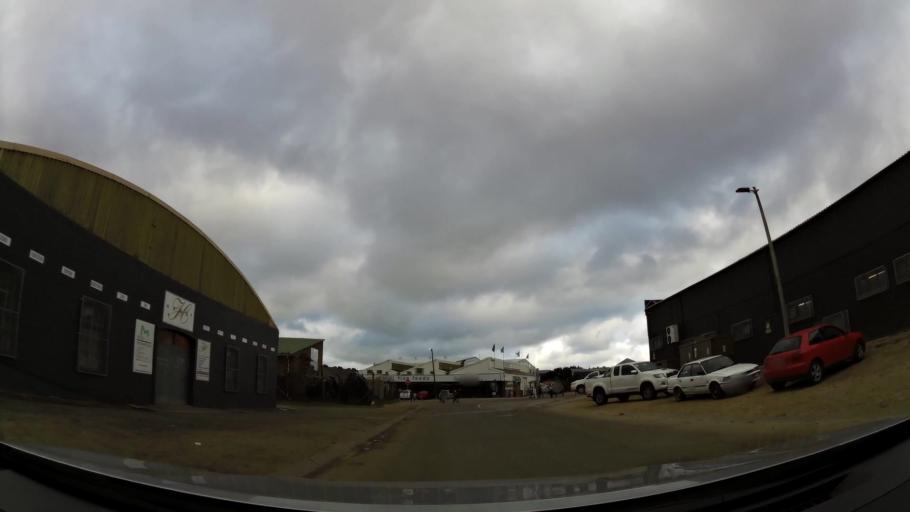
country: ZA
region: Western Cape
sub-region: Eden District Municipality
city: Plettenberg Bay
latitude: -34.0485
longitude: 23.3560
